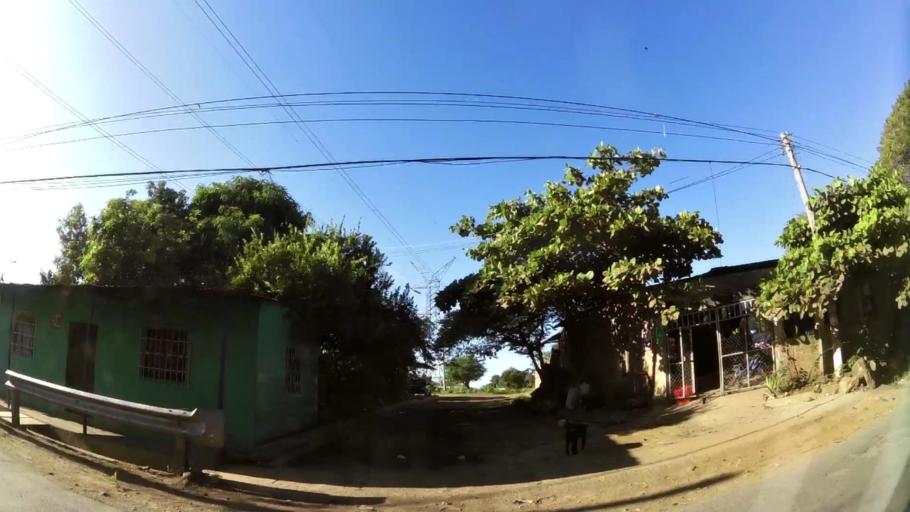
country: SV
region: Sonsonate
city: Sonsonate
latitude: 13.7067
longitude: -89.7161
